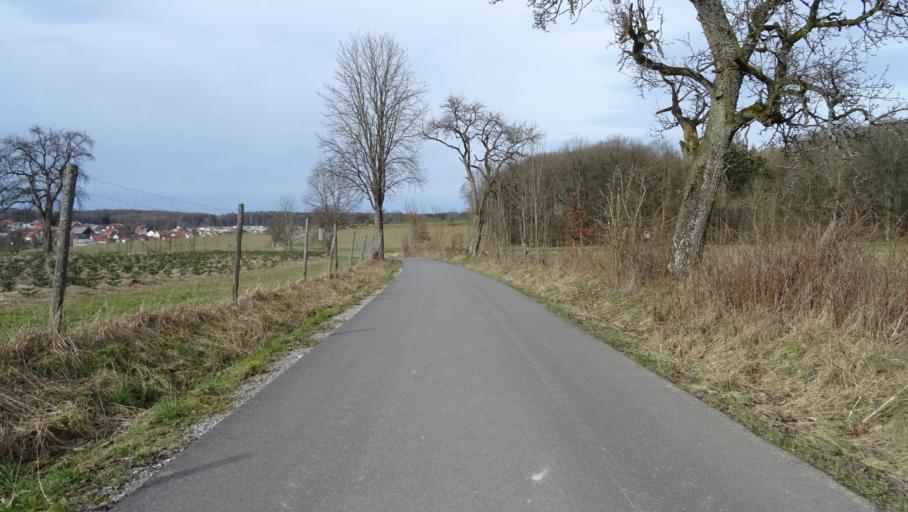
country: DE
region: Baden-Wuerttemberg
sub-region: Karlsruhe Region
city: Limbach
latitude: 49.4476
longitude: 9.2550
